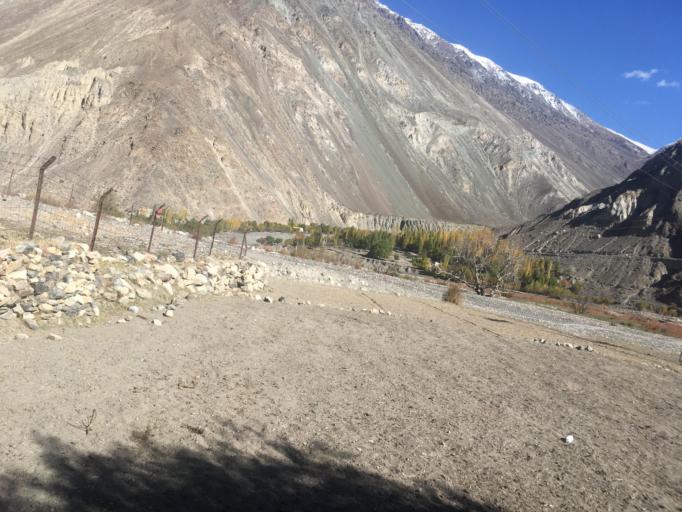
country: PK
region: Gilgit-Baltistan
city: Skardu
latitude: 35.1920
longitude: 75.6165
